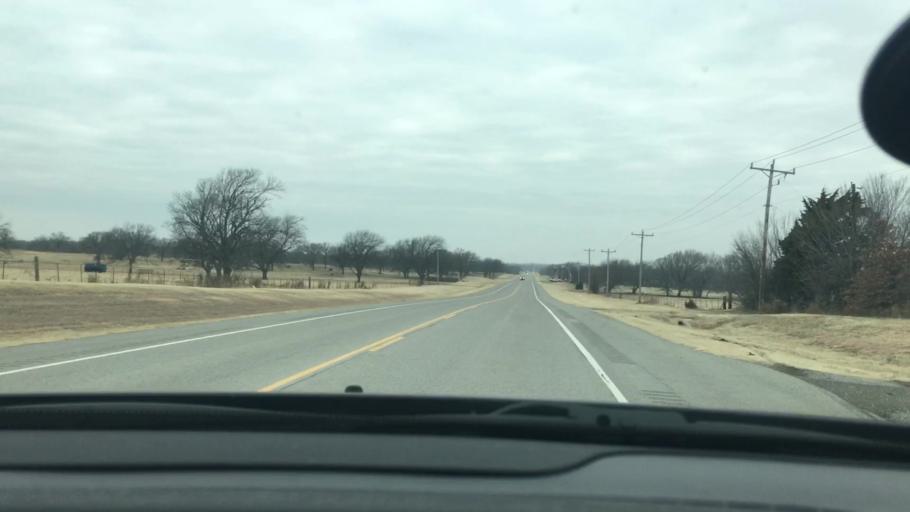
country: US
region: Oklahoma
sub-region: Carter County
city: Healdton
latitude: 34.4924
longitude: -97.4155
